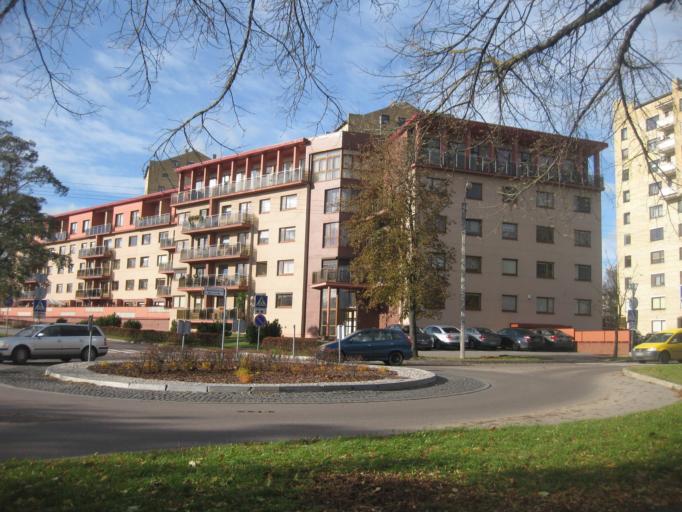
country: LT
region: Kauno apskritis
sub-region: Kaunas
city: Eiguliai
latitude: 54.9080
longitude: 23.9418
